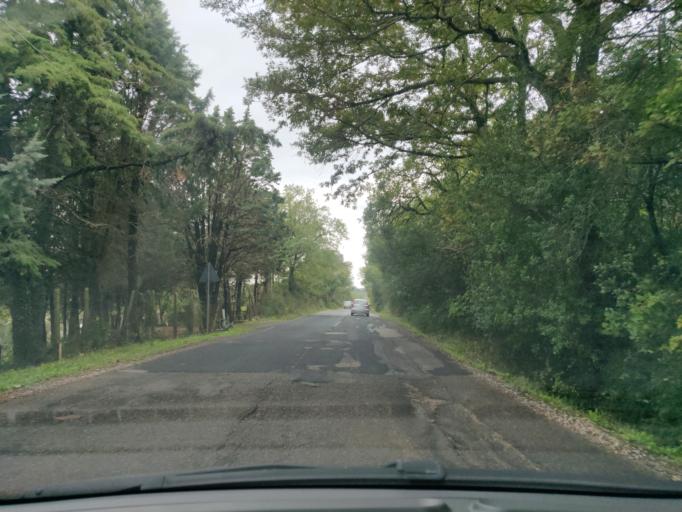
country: IT
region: Latium
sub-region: Citta metropolitana di Roma Capitale
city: Allumiere
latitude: 42.1291
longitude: 11.8662
